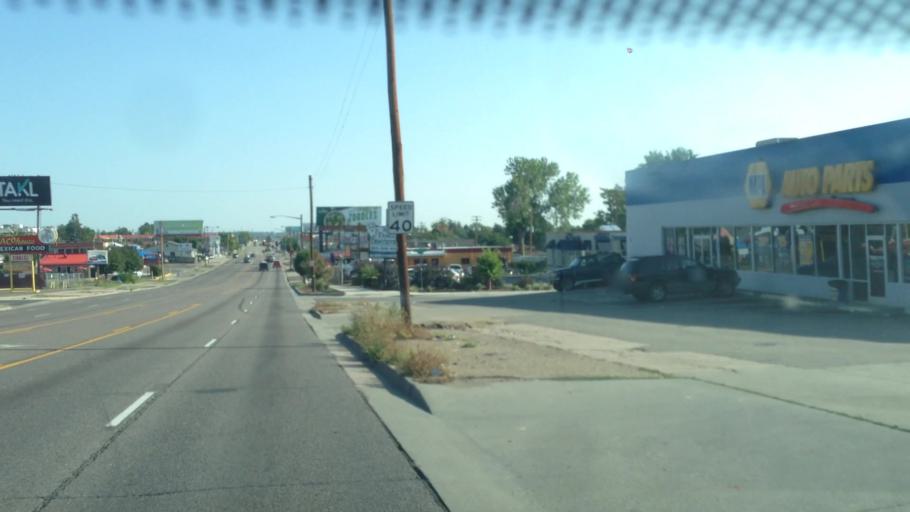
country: US
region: Colorado
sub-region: Denver County
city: Denver
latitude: 39.7051
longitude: -105.0251
